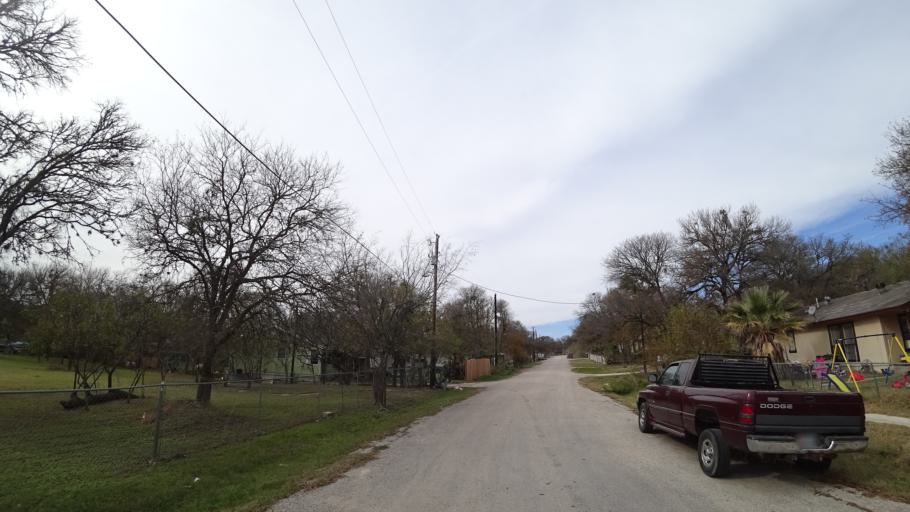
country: US
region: Texas
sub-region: Travis County
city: Garfield
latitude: 30.1329
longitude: -97.5691
